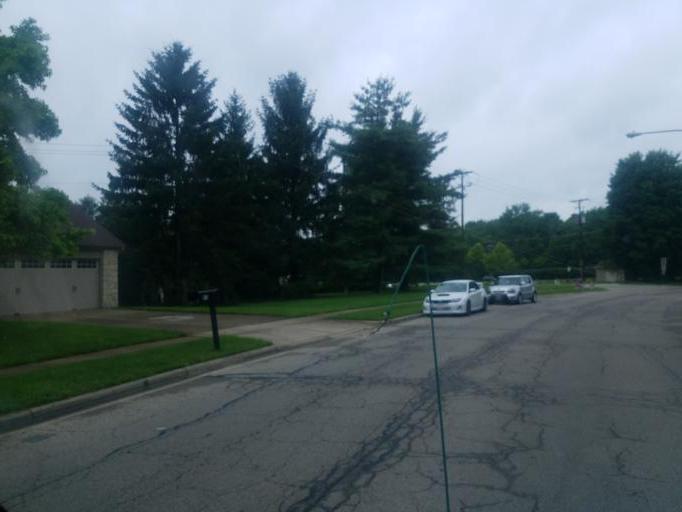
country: US
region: Ohio
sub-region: Franklin County
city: Gahanna
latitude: 40.0165
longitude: -82.8520
